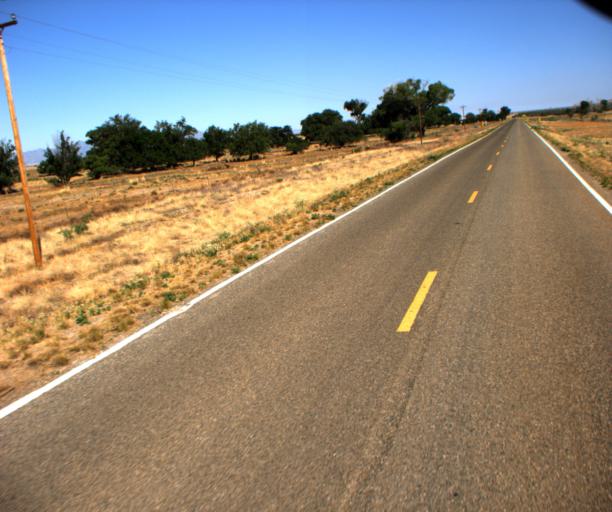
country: US
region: Arizona
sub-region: Graham County
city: Swift Trail Junction
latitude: 32.5857
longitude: -109.9632
